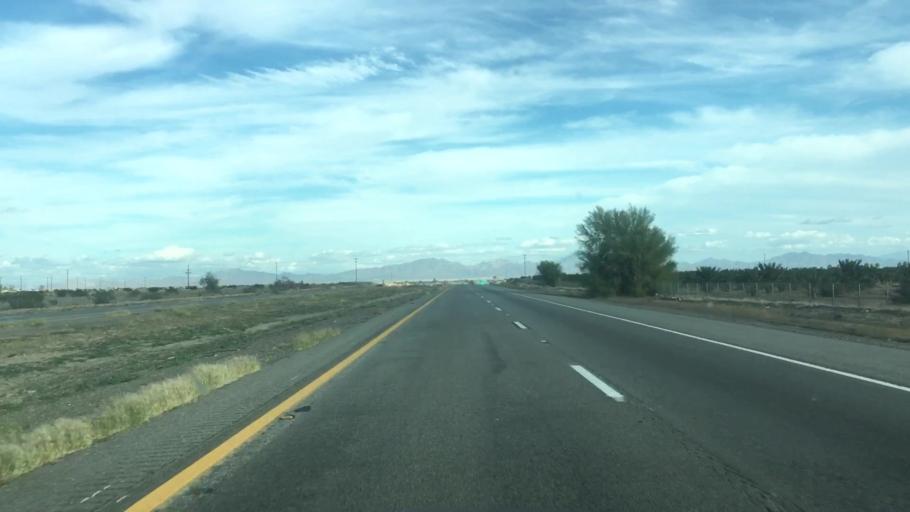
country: US
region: California
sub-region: Riverside County
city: Mesa Verde
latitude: 33.6066
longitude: -114.6863
